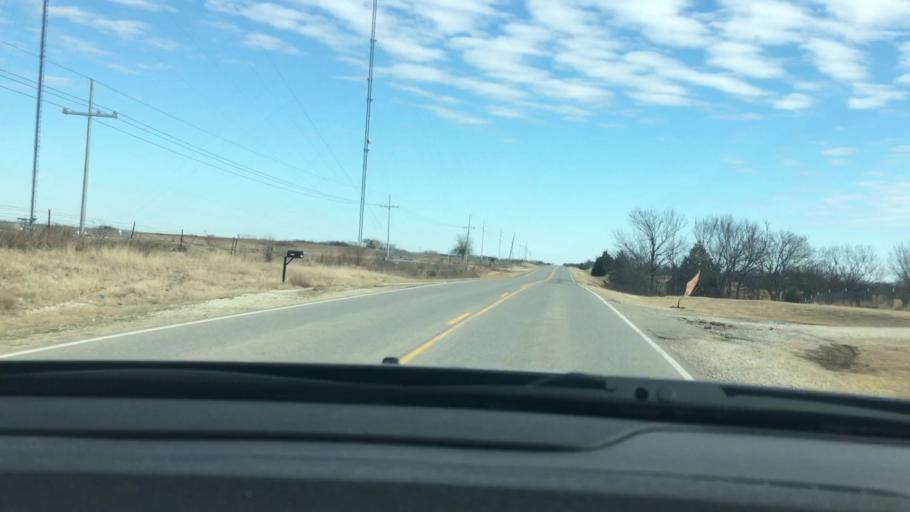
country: US
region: Oklahoma
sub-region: Garvin County
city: Stratford
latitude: 34.7967
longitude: -96.8871
